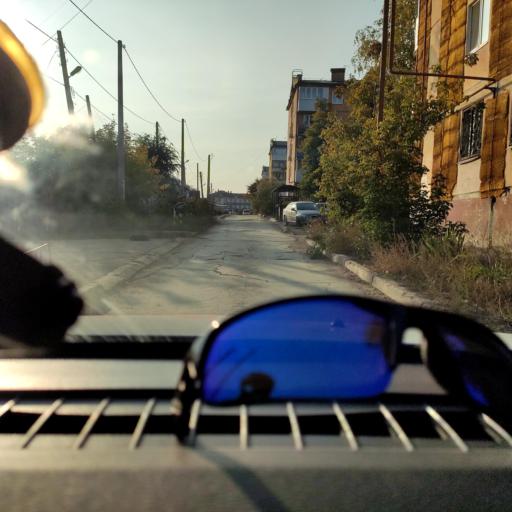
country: RU
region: Samara
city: Samara
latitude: 53.1998
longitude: 50.2072
